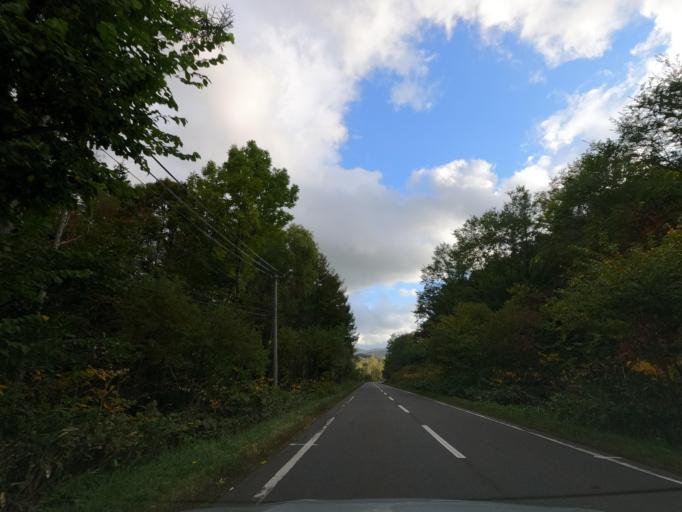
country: JP
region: Hokkaido
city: Date
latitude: 42.6570
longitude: 141.0685
